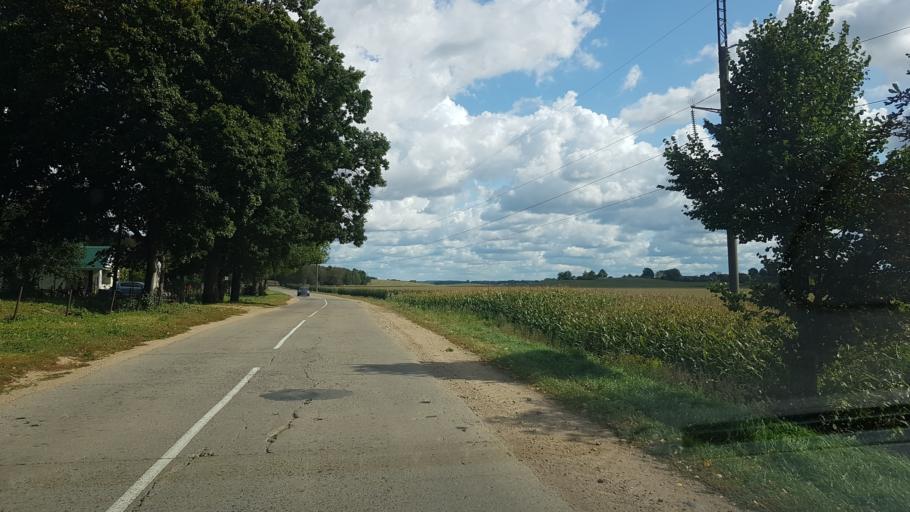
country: BY
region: Minsk
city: Dzyarzhynsk
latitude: 53.7354
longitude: 27.2243
